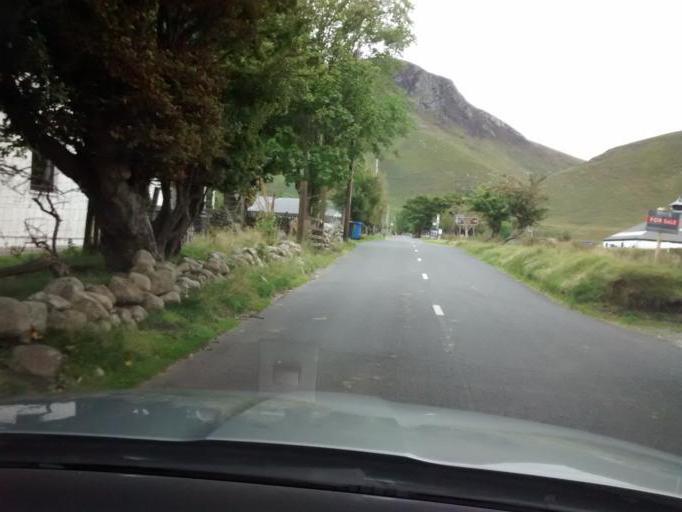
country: GB
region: Scotland
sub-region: North Ayrshire
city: Isle of Arran
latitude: 55.6992
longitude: -5.2773
